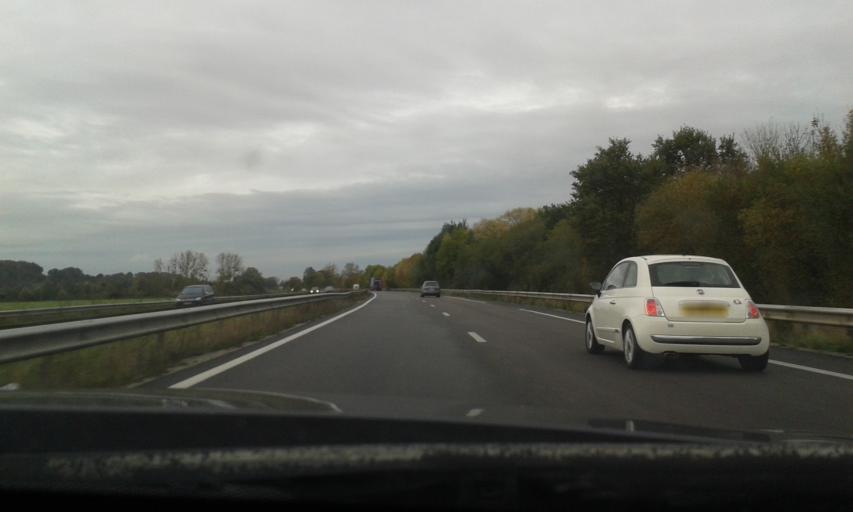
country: FR
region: Haute-Normandie
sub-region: Departement de l'Eure
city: Heudreville-sur-Eure
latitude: 49.1511
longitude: 1.1826
